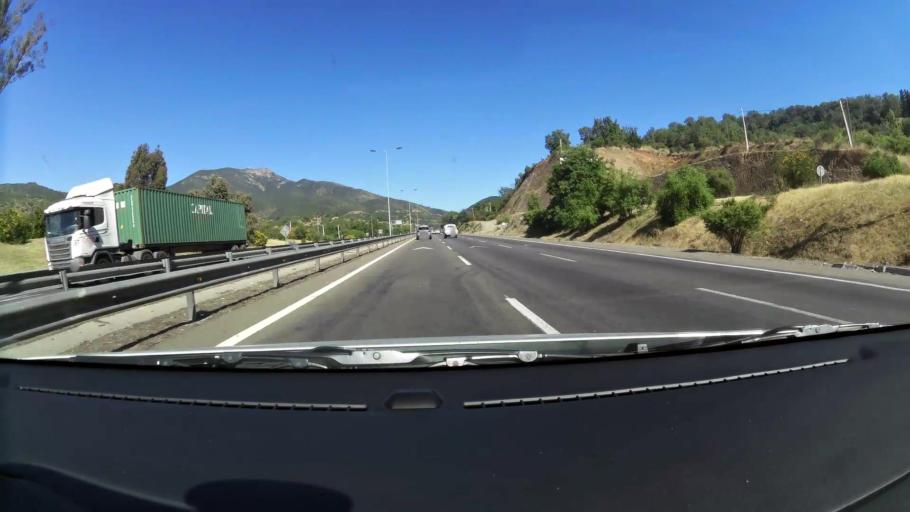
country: CL
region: Santiago Metropolitan
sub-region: Provincia de Melipilla
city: Melipilla
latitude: -33.3960
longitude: -71.2365
